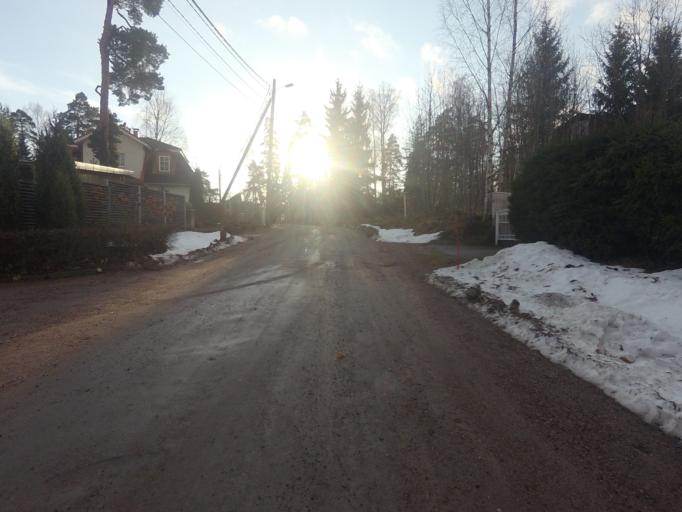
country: FI
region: Uusimaa
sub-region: Helsinki
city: Teekkarikylae
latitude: 60.2047
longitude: 24.8274
